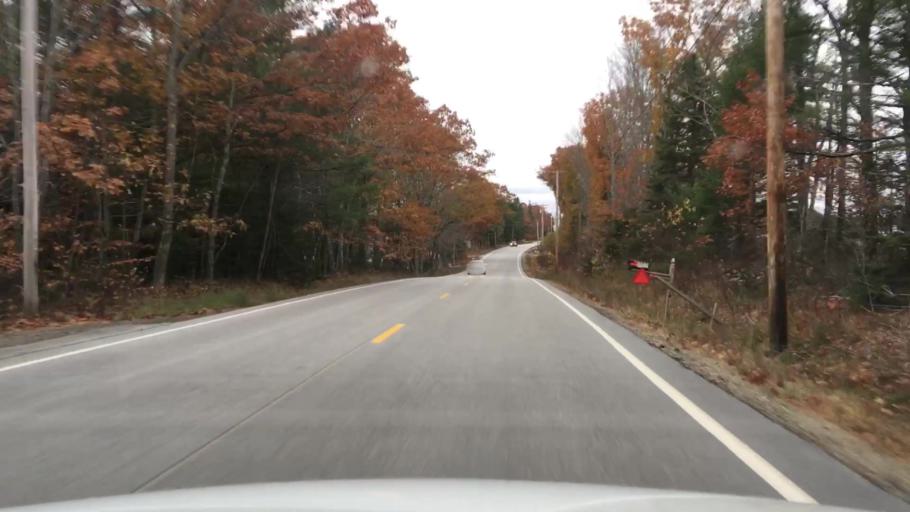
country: US
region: Maine
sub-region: Hancock County
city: Orland
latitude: 44.5405
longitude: -68.6831
